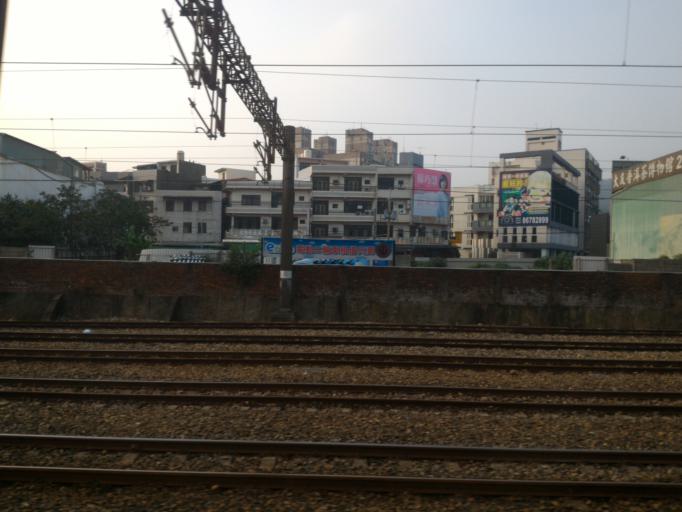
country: TW
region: Taiwan
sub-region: Taoyuan
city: Taoyuan
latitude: 24.9539
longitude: 121.3543
